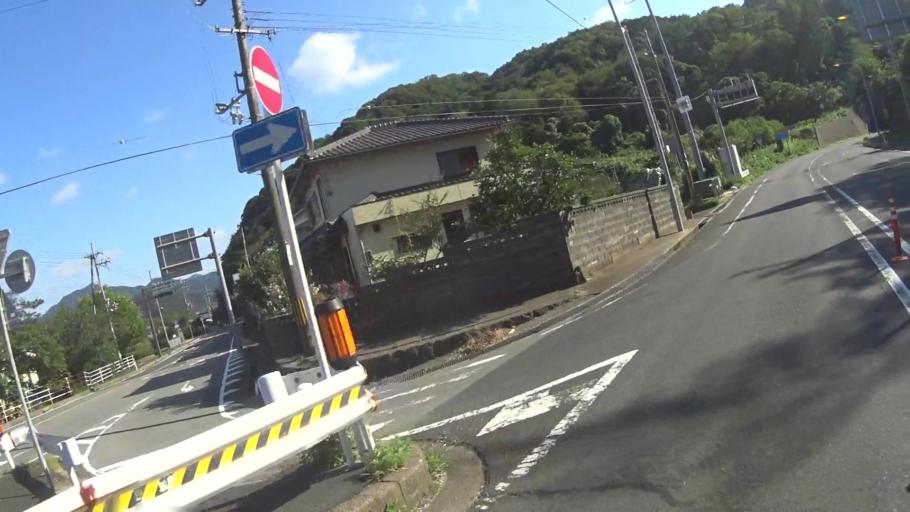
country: JP
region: Kyoto
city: Miyazu
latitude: 35.7308
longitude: 135.0958
